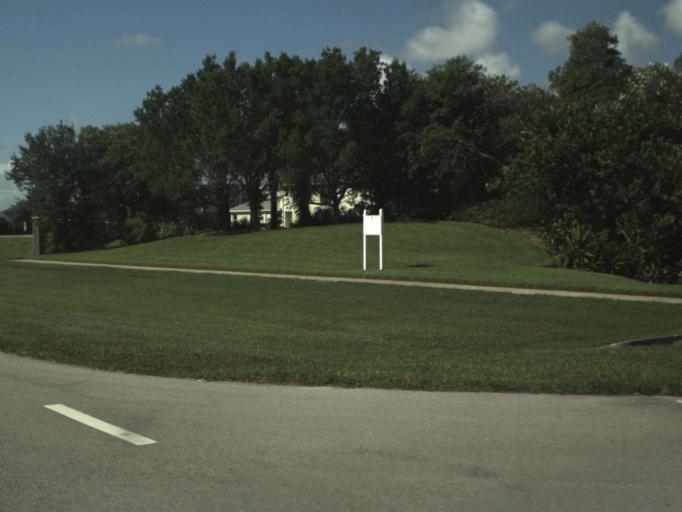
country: US
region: Florida
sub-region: Indian River County
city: Gifford
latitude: 27.6766
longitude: -80.4012
